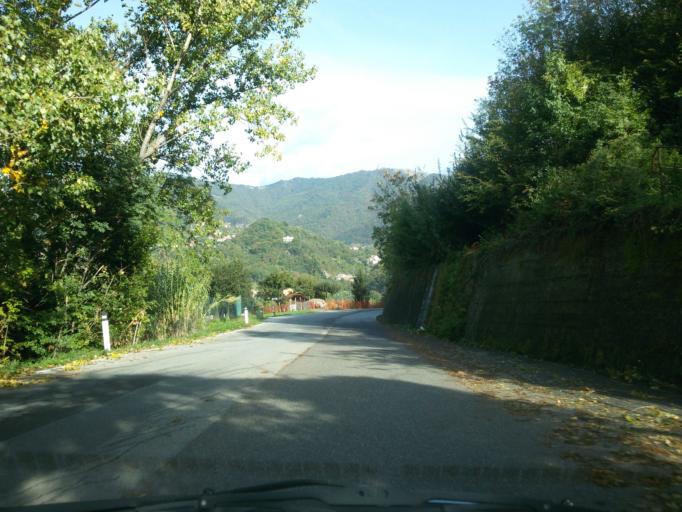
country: IT
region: Liguria
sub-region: Provincia di Genova
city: Piccarello
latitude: 44.4800
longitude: 8.9630
